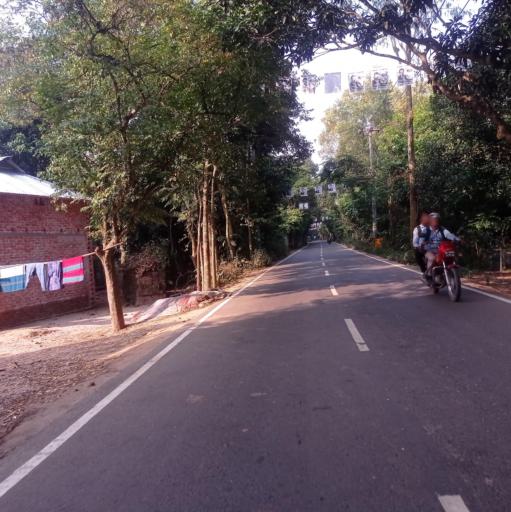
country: BD
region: Dhaka
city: Bhairab Bazar
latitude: 24.0512
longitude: 90.8352
